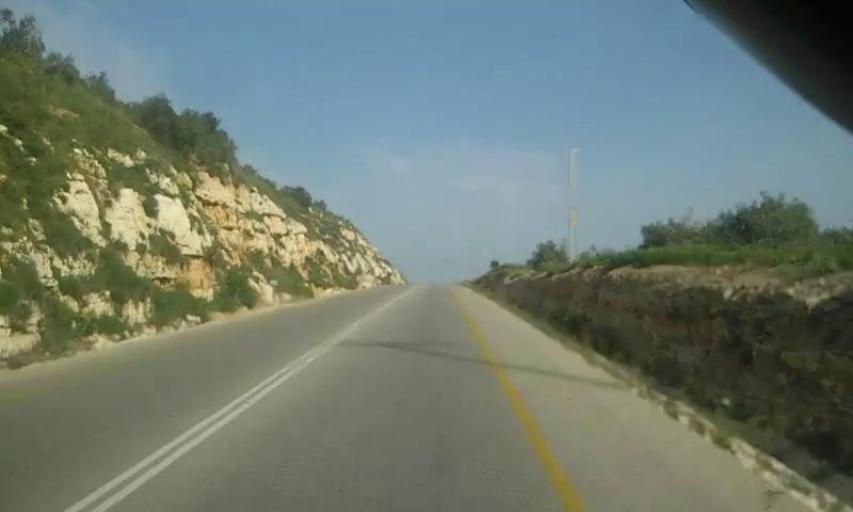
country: PS
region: West Bank
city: Till
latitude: 32.1907
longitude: 35.2055
